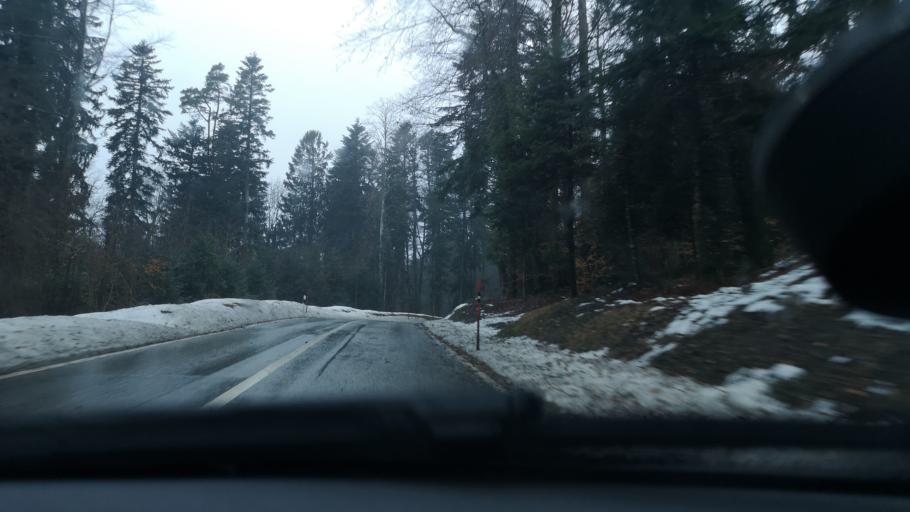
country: CH
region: Neuchatel
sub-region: Val-de-Ruz District
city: Les Geneveys-sur-Coffrane
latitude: 46.9835
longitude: 6.8440
